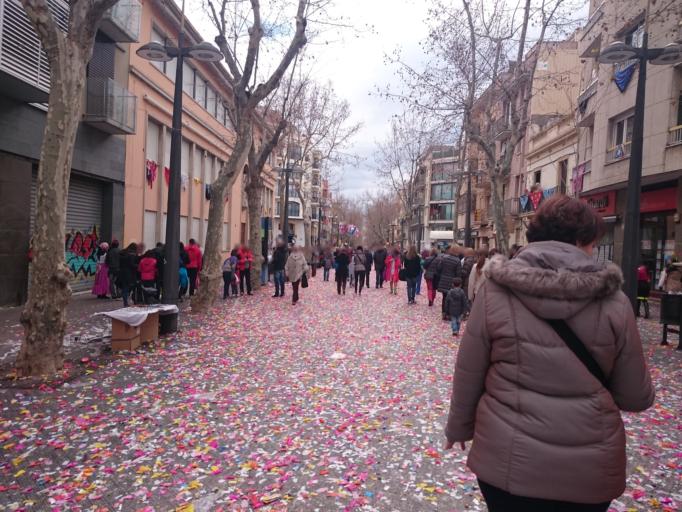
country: ES
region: Catalonia
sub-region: Provincia de Barcelona
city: Vilanova i la Geltru
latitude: 41.2215
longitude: 1.7262
